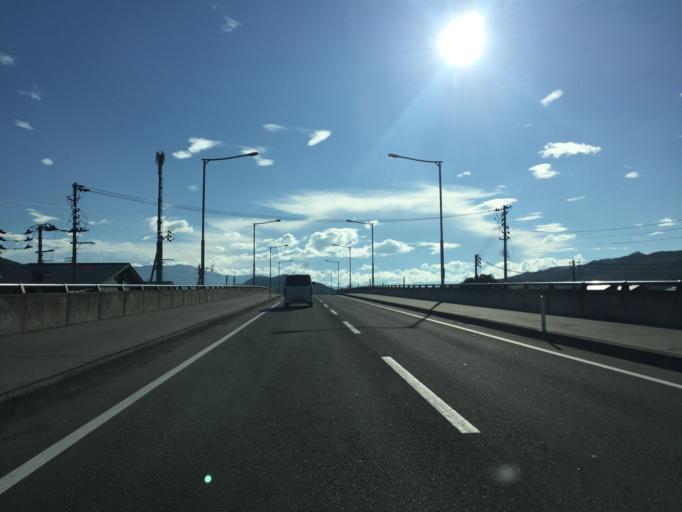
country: JP
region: Yamagata
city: Yonezawa
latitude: 37.9205
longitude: 140.0848
